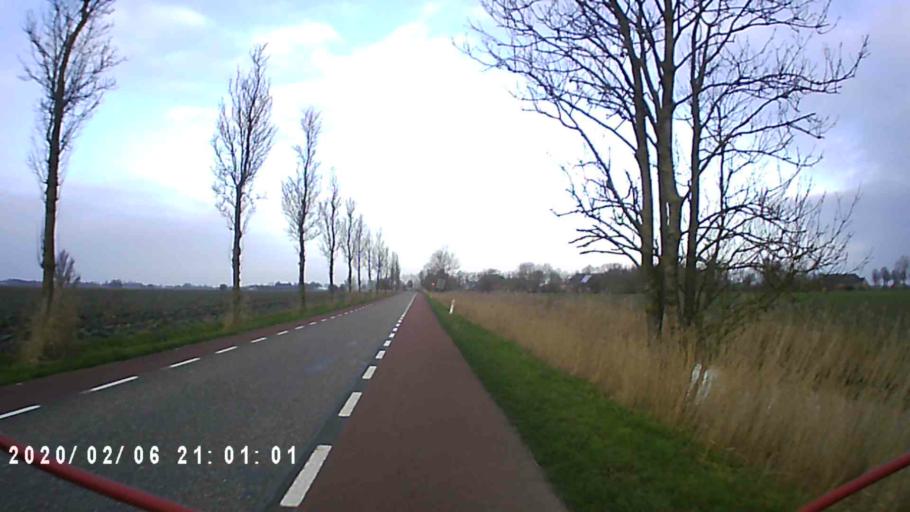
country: NL
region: Groningen
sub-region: Gemeente Zuidhorn
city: Oldehove
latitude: 53.3112
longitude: 6.4250
